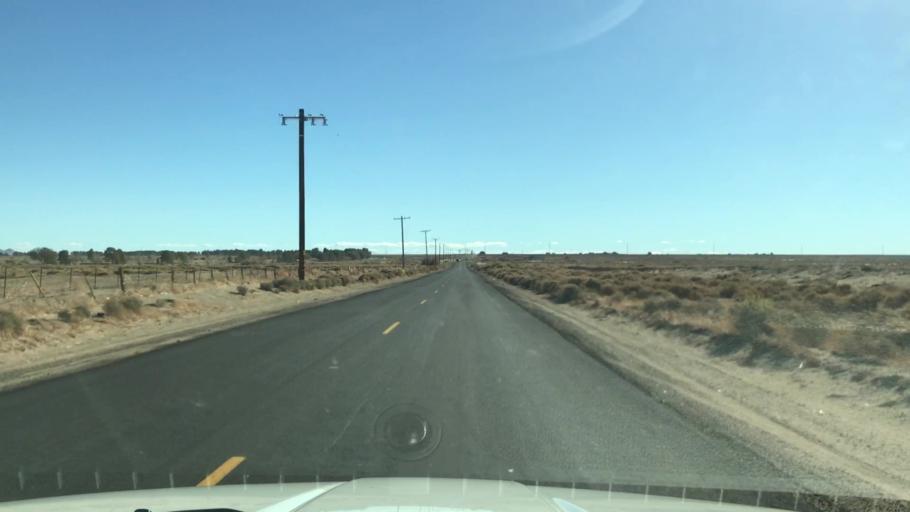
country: US
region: California
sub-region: Kern County
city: California City
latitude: 35.2789
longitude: -117.9857
